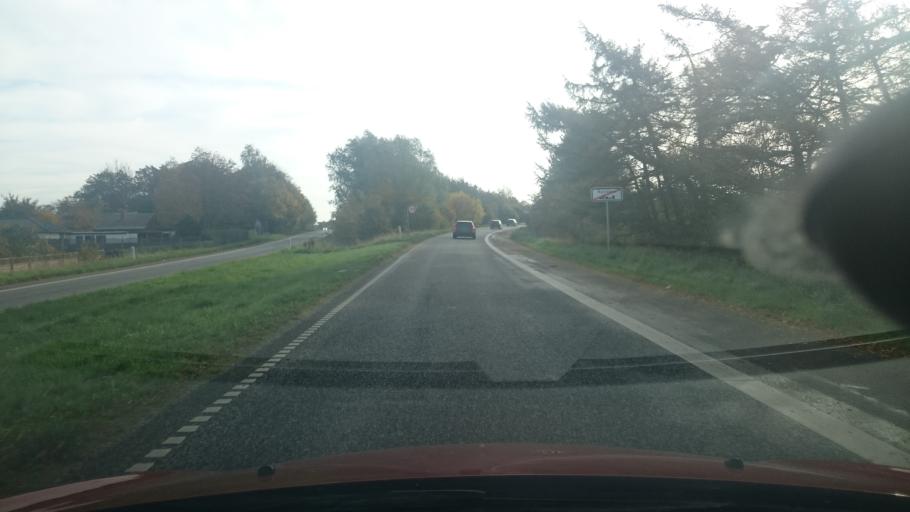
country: DK
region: Central Jutland
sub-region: Randers Kommune
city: Randers
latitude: 56.4432
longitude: 10.0779
